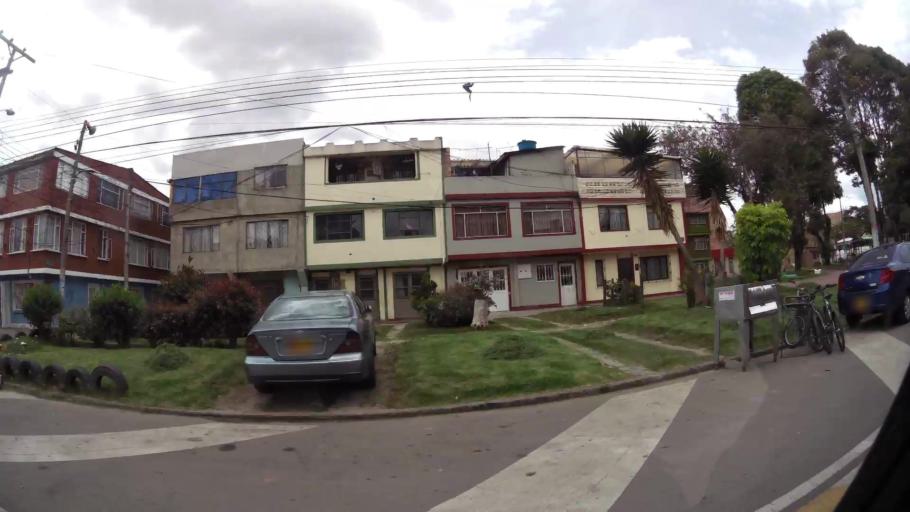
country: CO
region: Cundinamarca
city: Funza
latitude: 4.7111
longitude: -74.1228
